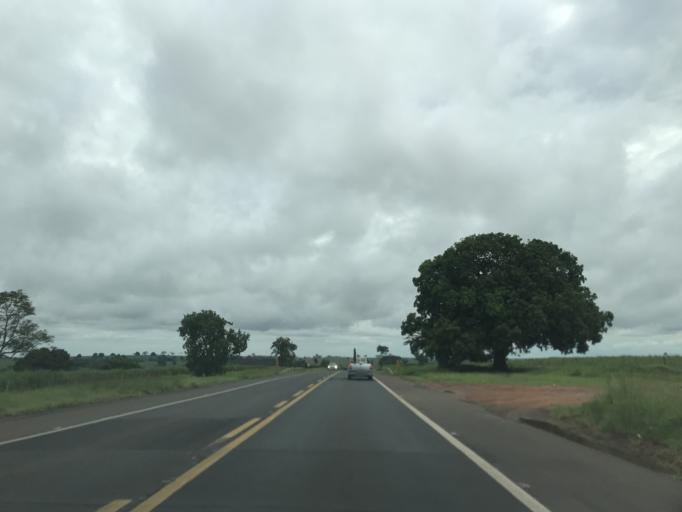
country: BR
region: Sao Paulo
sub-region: Nova Granada
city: Nova Granada
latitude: -20.4848
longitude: -49.3042
